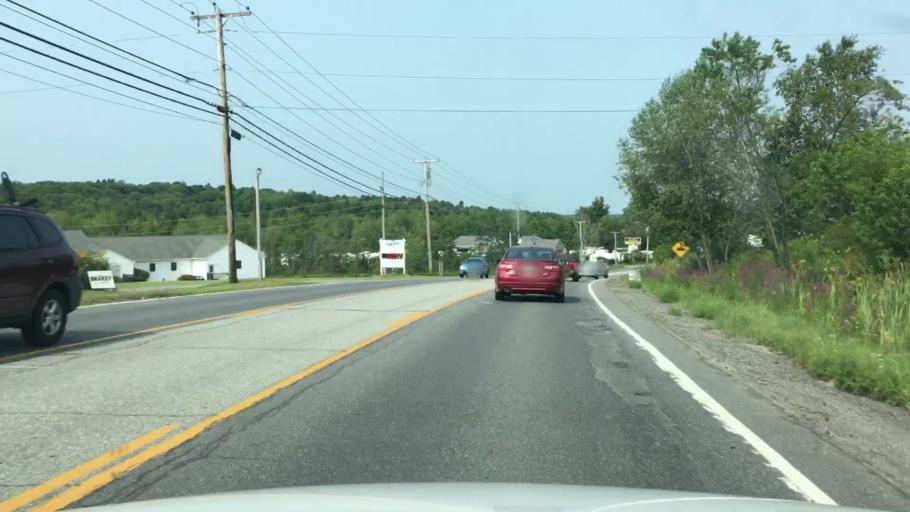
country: US
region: Maine
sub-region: Kennebec County
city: Manchester
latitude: 44.3214
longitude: -69.8422
